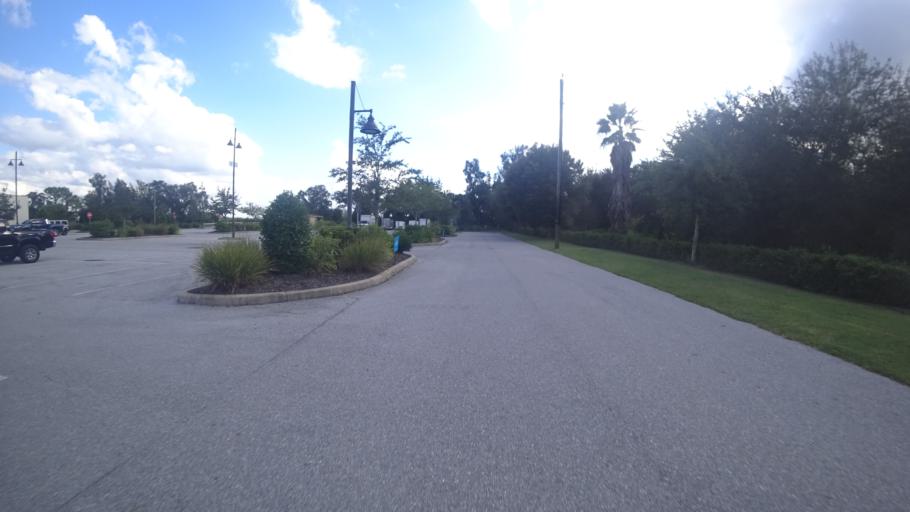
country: US
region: Florida
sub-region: Sarasota County
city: The Meadows
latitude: 27.4727
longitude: -82.3833
